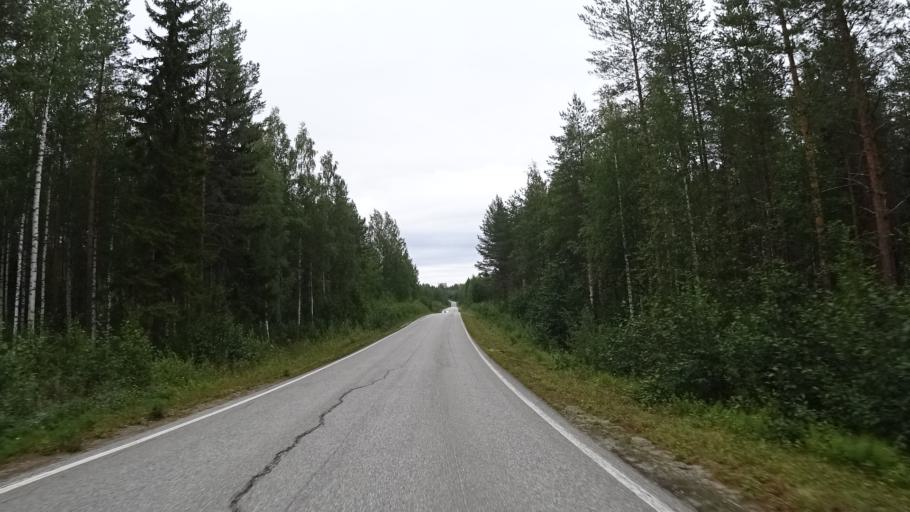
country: FI
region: North Karelia
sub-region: Pielisen Karjala
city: Lieksa
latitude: 63.3687
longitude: 30.2929
